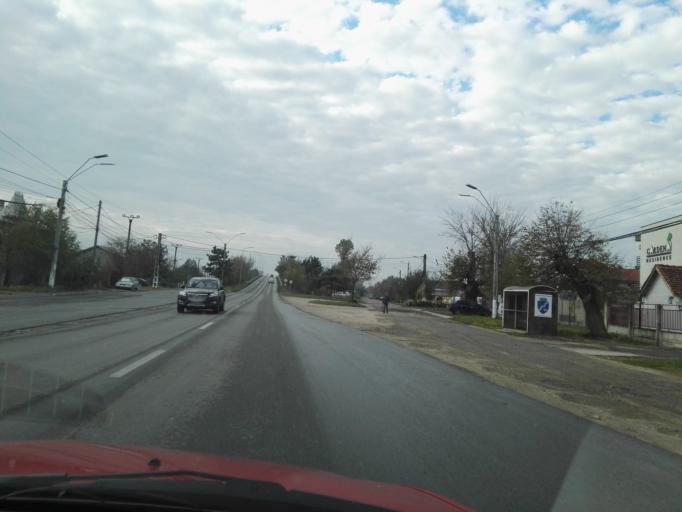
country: RO
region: Ilfov
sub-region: Comuna Magurele
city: Magurele
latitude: 44.3620
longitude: 26.0382
